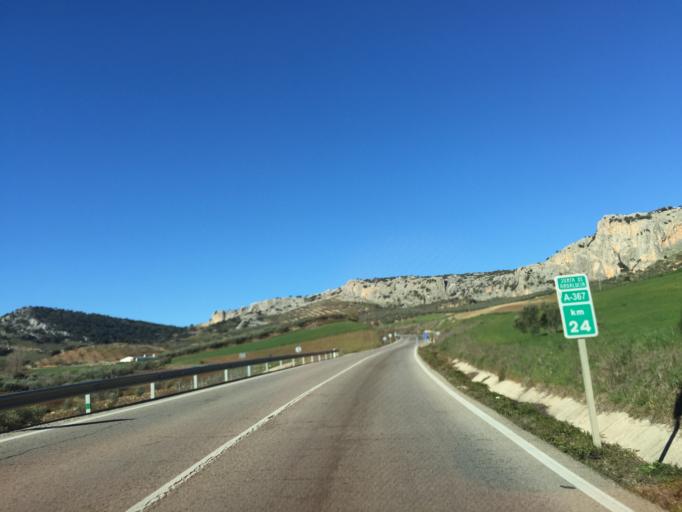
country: ES
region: Andalusia
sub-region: Provincia de Malaga
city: Cuevas del Becerro
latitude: 36.8643
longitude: -5.0540
